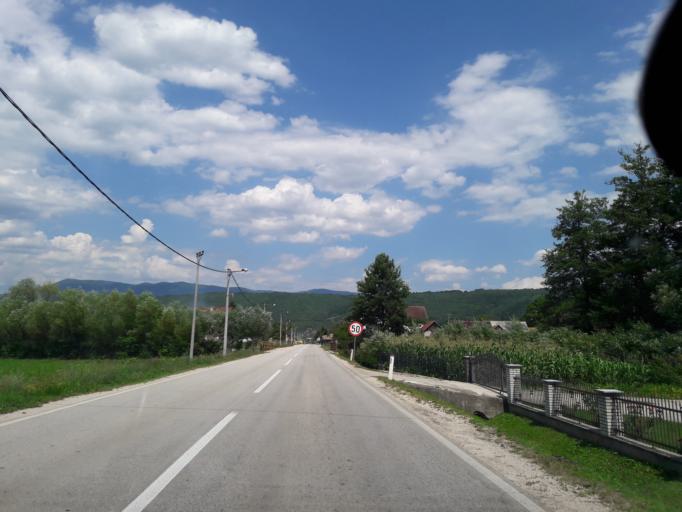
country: BA
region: Republika Srpska
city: Mrkonjic Grad
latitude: 44.4338
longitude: 17.1451
